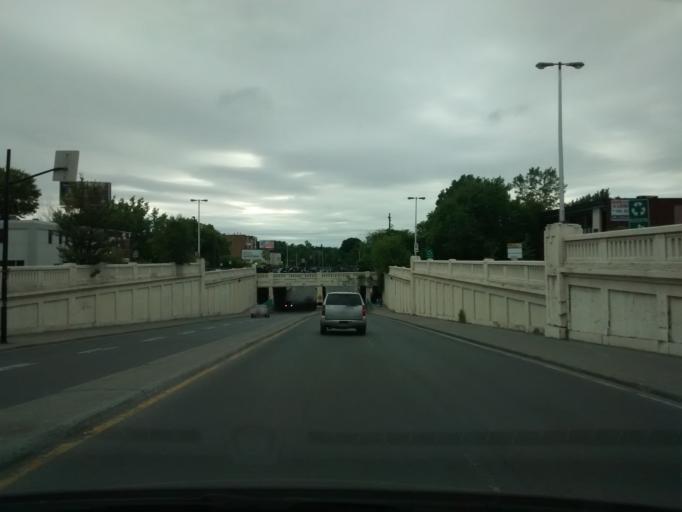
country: CA
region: Quebec
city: Mont-Royal
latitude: 45.5038
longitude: -73.6388
